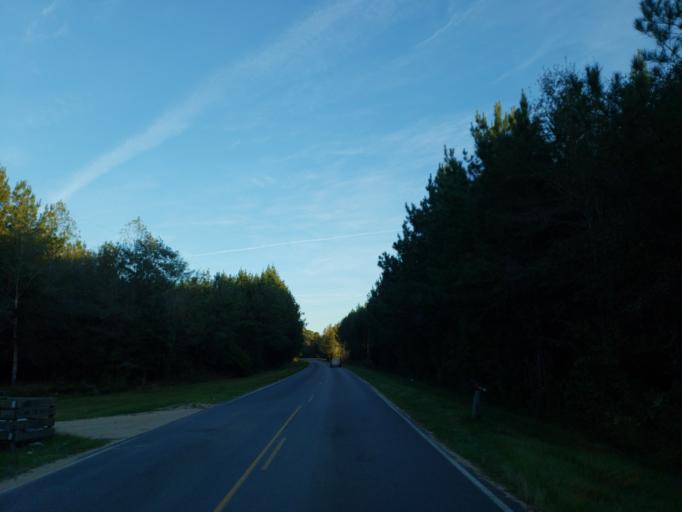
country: US
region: Mississippi
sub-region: Wayne County
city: Belmont
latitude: 31.4393
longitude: -88.4991
